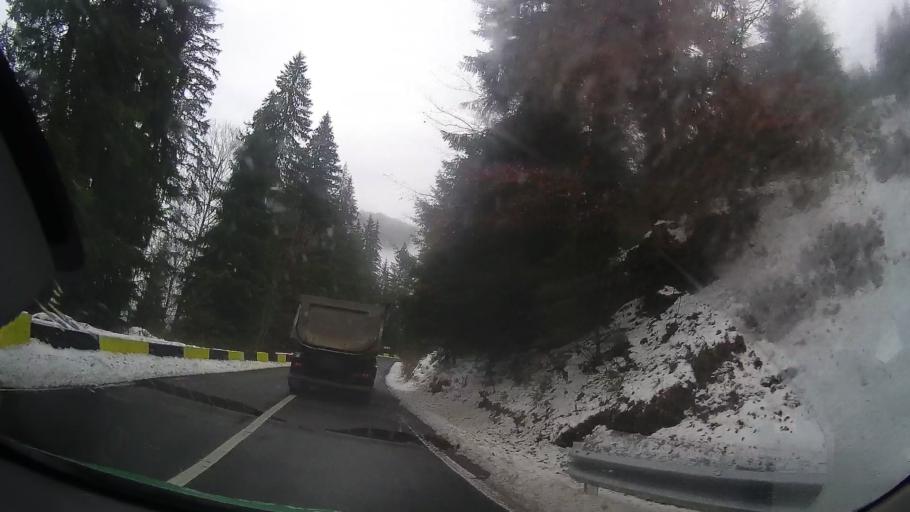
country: RO
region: Harghita
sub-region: Oras Balan
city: Balan
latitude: 46.7783
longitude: 25.7427
